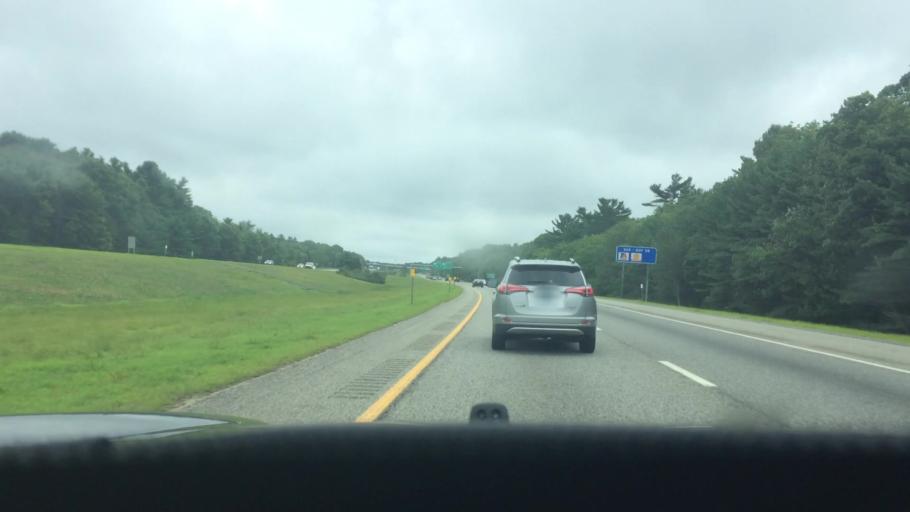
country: US
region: Rhode Island
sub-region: Kent County
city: West Greenwich
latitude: 41.6120
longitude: -71.6538
